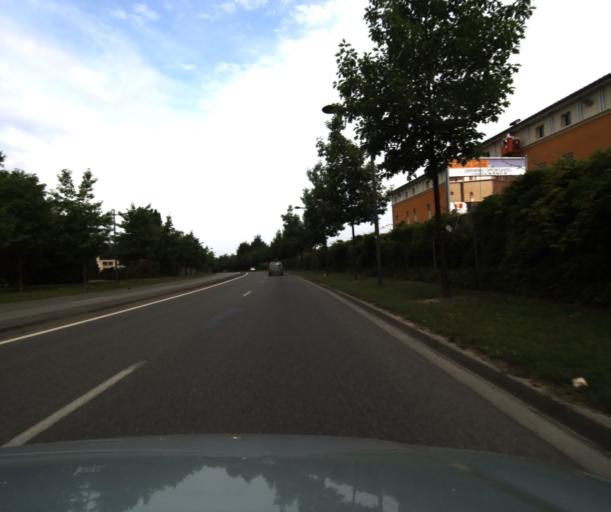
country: FR
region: Midi-Pyrenees
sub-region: Departement des Hautes-Pyrenees
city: Laloubere
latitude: 43.2221
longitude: 0.0568
